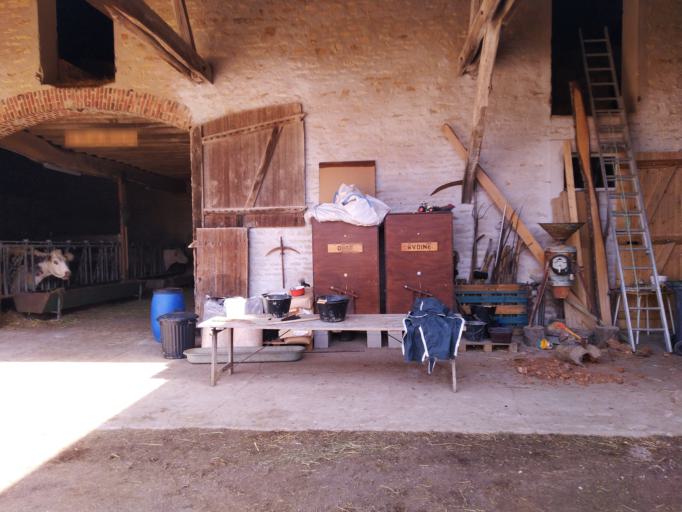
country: FR
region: Bourgogne
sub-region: Departement de l'Yonne
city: Avallon
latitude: 47.5623
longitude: 4.0613
